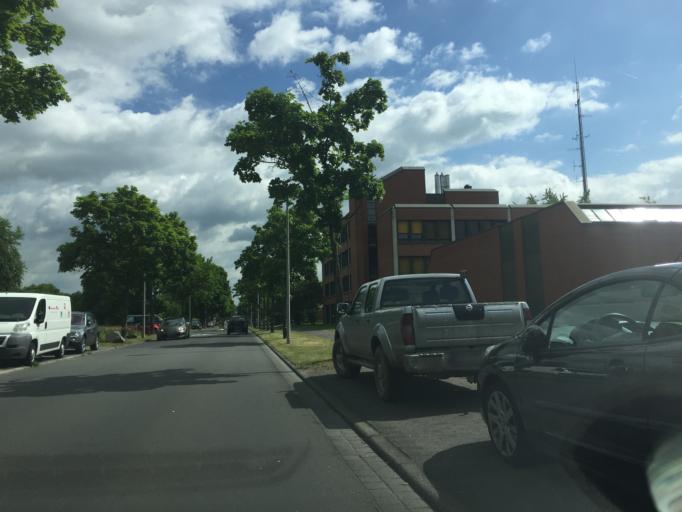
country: DE
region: Bavaria
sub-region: Regierungsbezirk Unterfranken
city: Aschaffenburg
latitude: 49.9630
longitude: 9.1265
